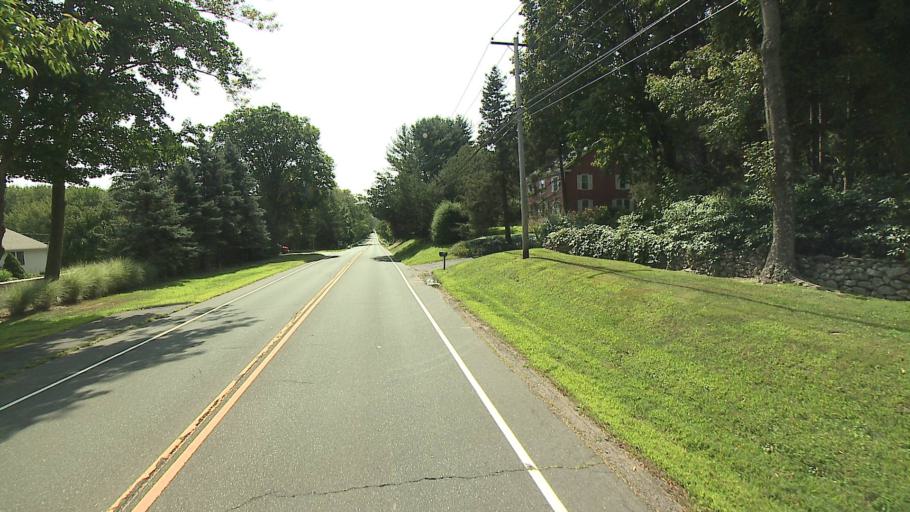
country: US
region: Connecticut
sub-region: Fairfield County
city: Trumbull
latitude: 41.2671
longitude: -73.2938
